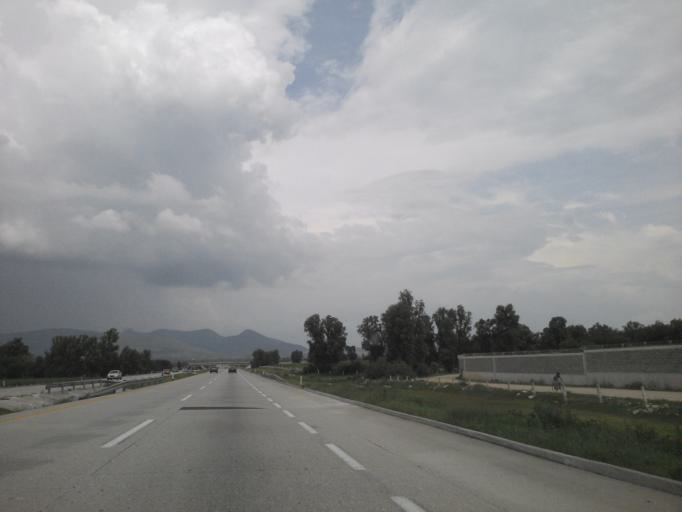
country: MX
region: Hidalgo
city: Doxey
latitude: 20.0763
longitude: -99.2386
